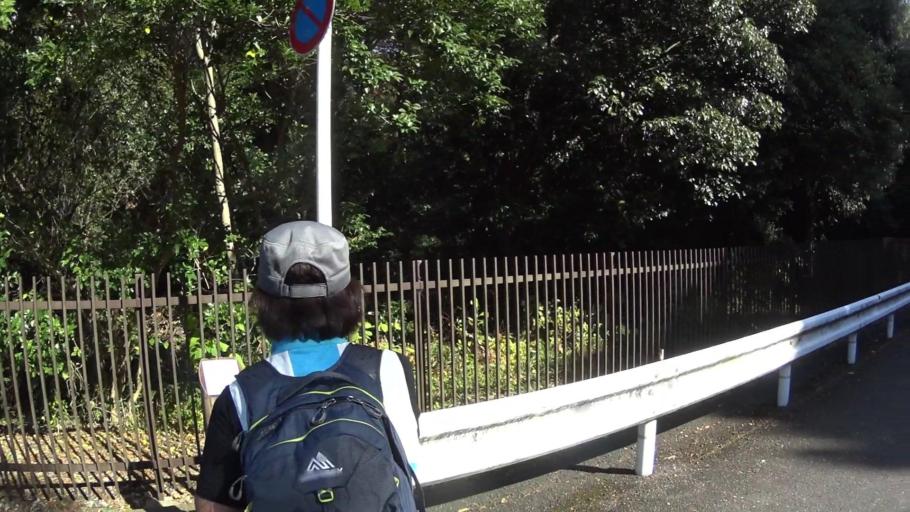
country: JP
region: Kyoto
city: Uji
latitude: 34.9385
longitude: 135.7746
